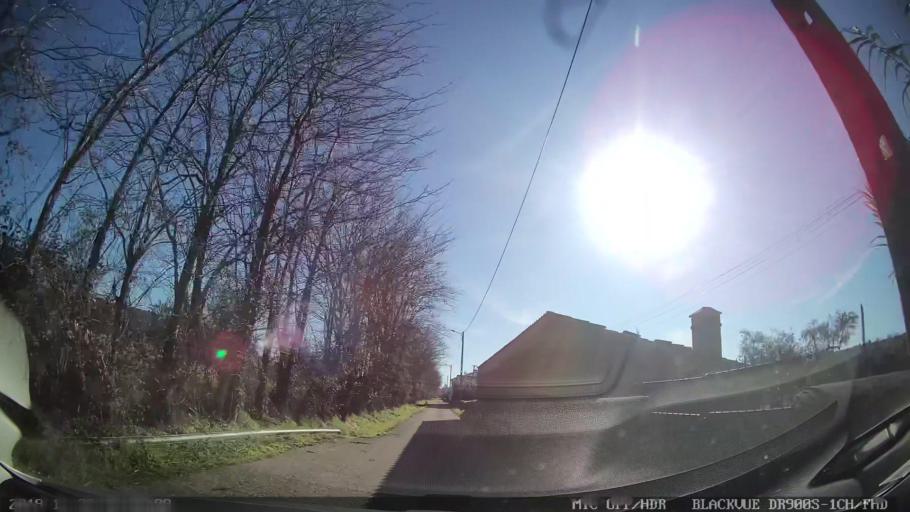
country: PT
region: Castelo Branco
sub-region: Idanha-A-Nova
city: Idanha-a-Nova
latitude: 39.9155
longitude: -7.2202
